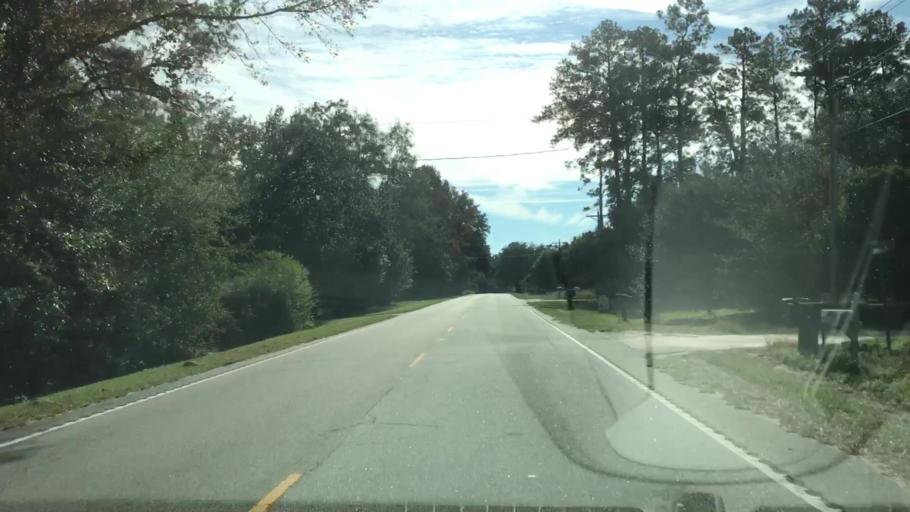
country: US
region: South Carolina
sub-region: Colleton County
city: Walterboro
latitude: 32.8514
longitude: -80.5954
